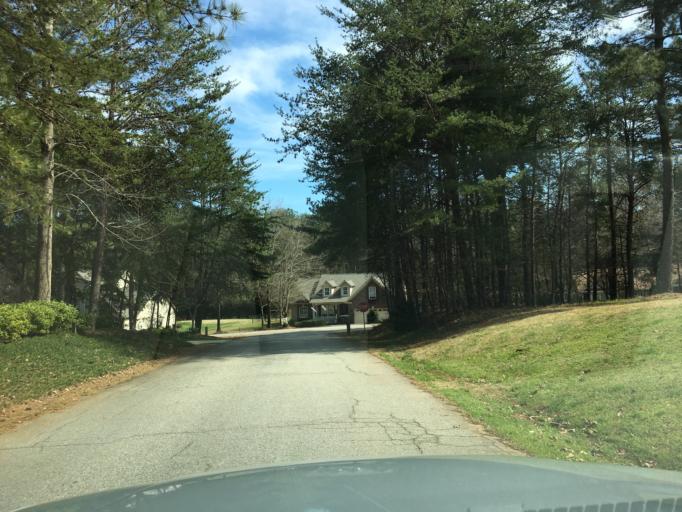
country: US
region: South Carolina
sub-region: Spartanburg County
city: Wellford
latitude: 34.9095
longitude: -82.0938
